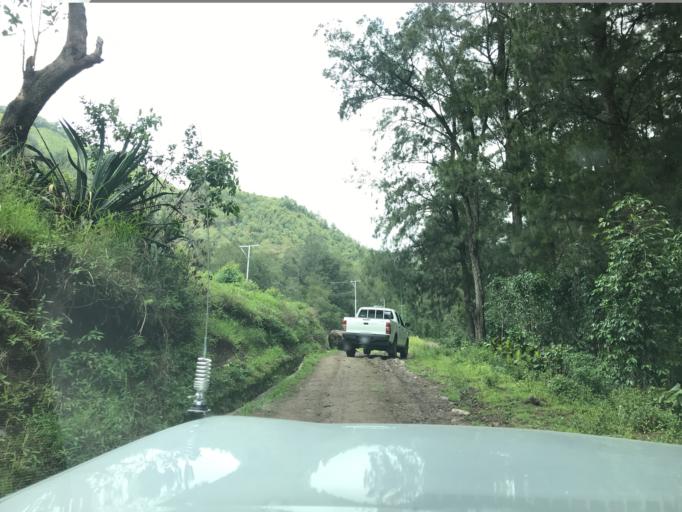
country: TL
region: Aileu
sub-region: Aileu Villa
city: Aileu
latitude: -8.8637
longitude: 125.5634
